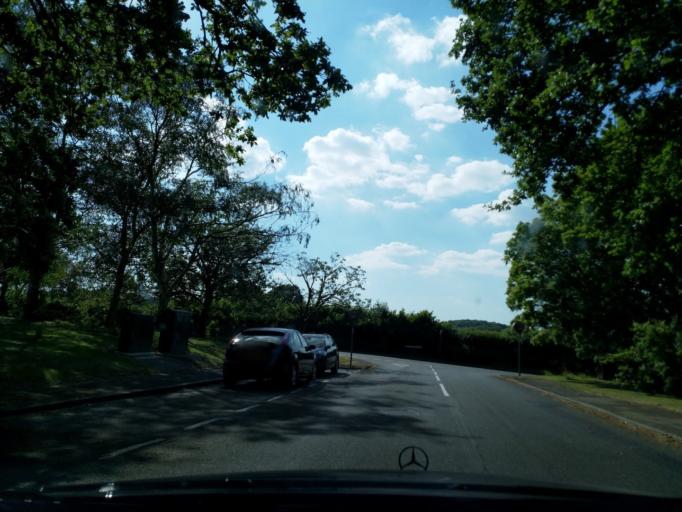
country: GB
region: England
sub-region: Warwickshire
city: Warwick
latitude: 52.2836
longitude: -1.6238
